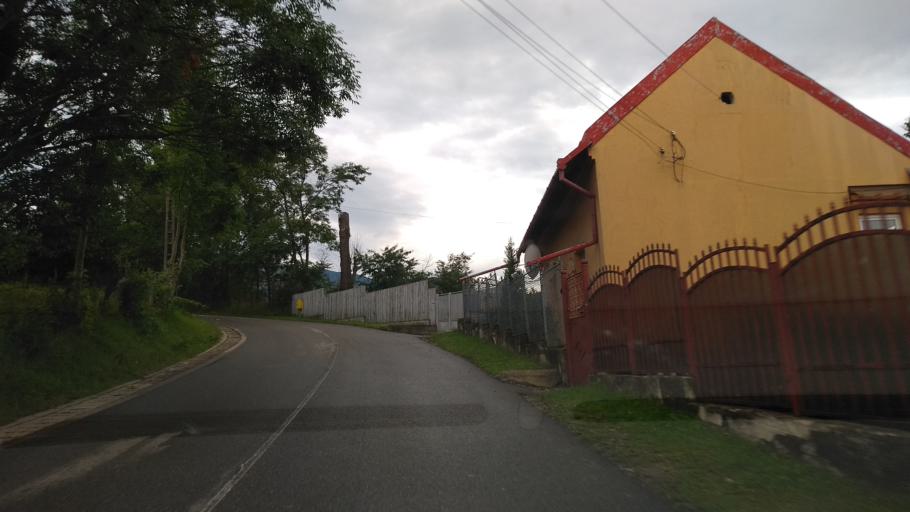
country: RO
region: Hunedoara
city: Vulcan
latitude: 45.3717
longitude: 23.2816
